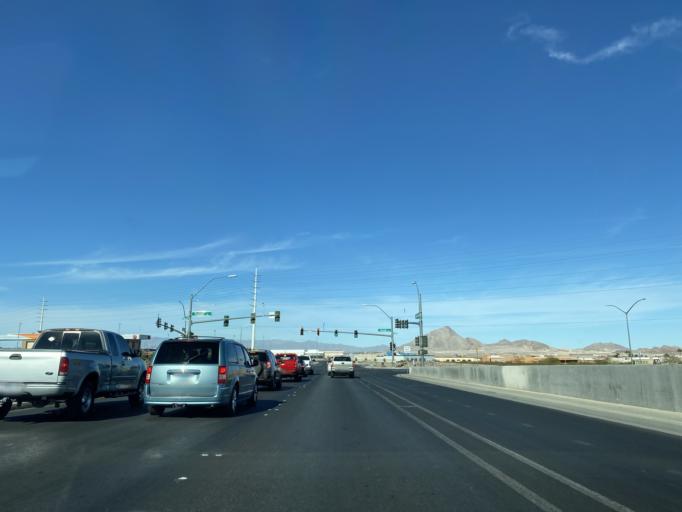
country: US
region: Nevada
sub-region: Clark County
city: Henderson
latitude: 36.0630
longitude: -115.0271
